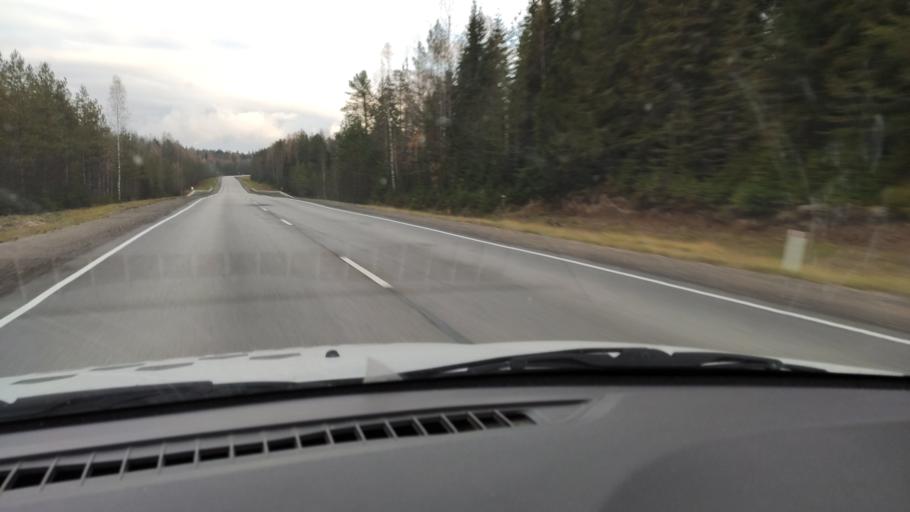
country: RU
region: Kirov
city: Chernaya Kholunitsa
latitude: 58.8237
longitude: 51.7957
